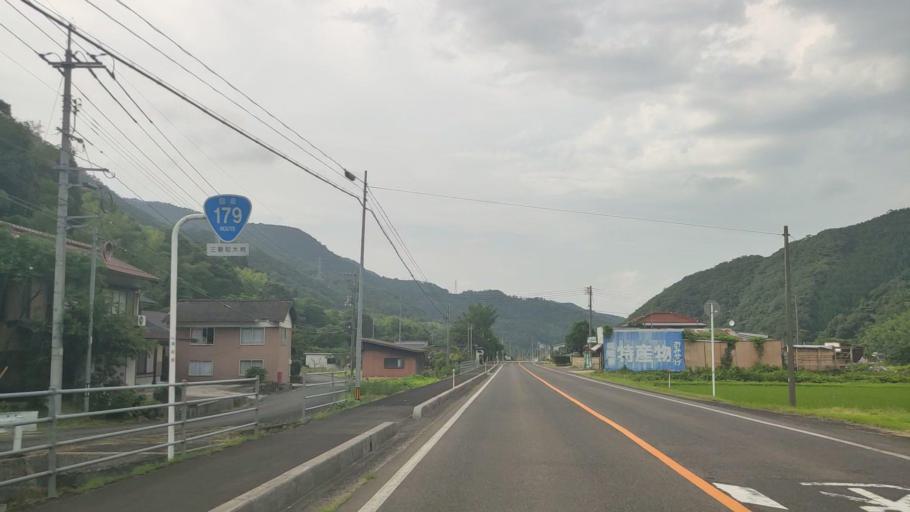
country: JP
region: Tottori
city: Kurayoshi
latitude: 35.3674
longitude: 133.8502
